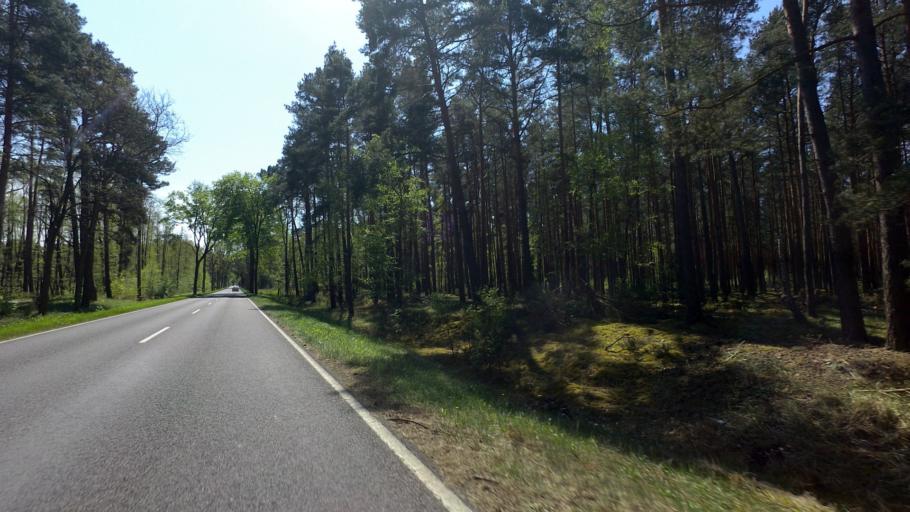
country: DE
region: Brandenburg
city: Halbe
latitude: 52.1406
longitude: 13.7486
